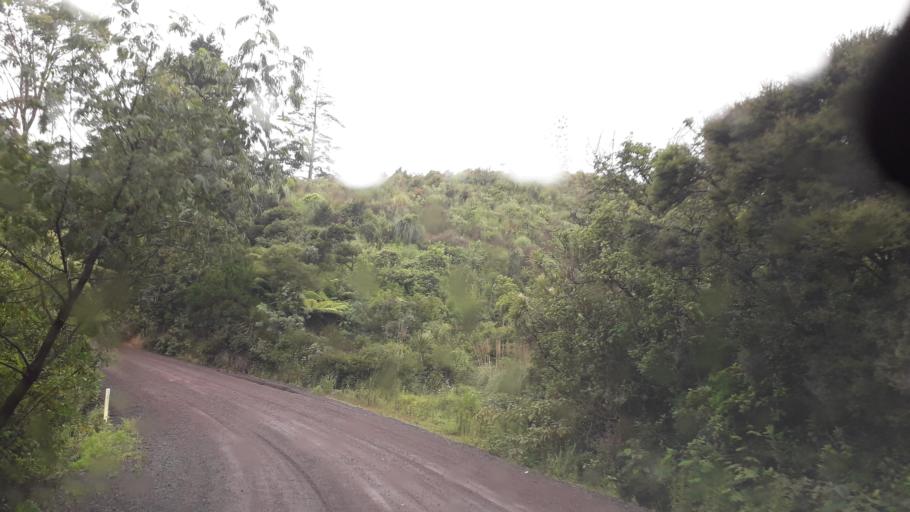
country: NZ
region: Northland
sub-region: Far North District
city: Paihia
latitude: -35.2394
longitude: 174.2538
